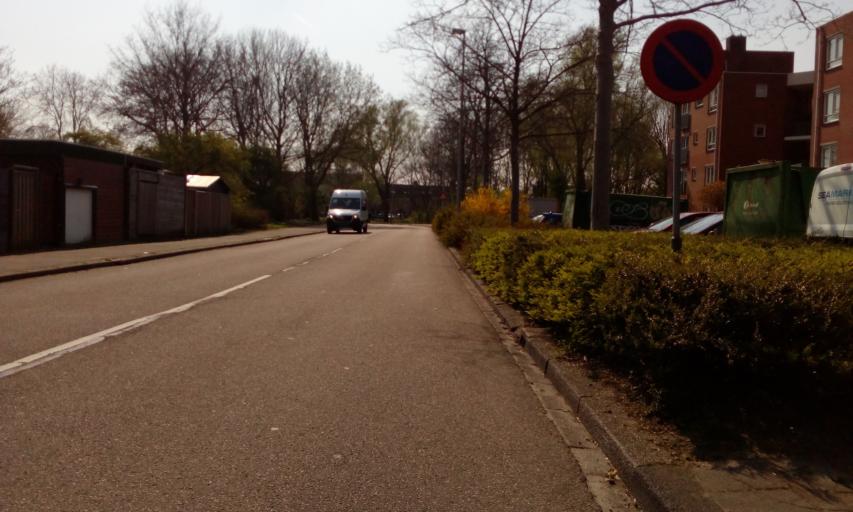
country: NL
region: South Holland
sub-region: Gemeente Spijkenisse
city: Spijkenisse
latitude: 51.8317
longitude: 4.3290
